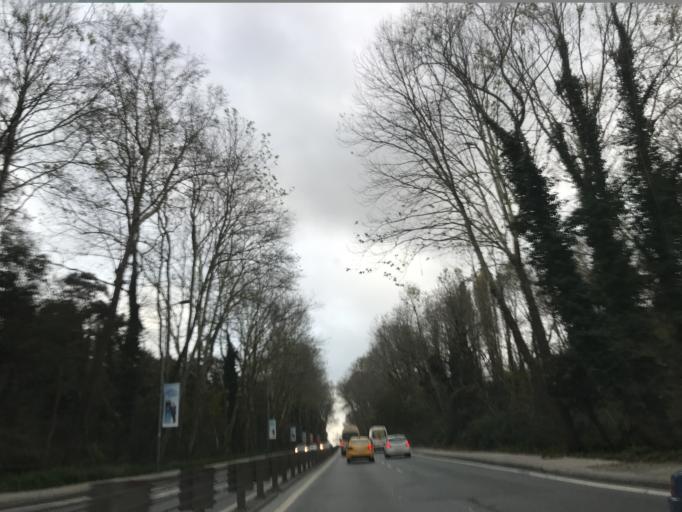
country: TR
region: Istanbul
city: Arikoey
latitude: 41.1467
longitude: 29.0278
